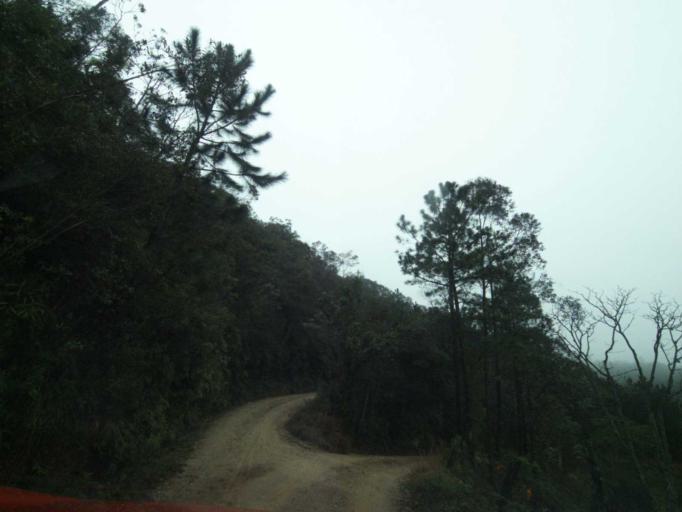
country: BR
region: Santa Catarina
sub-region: Anitapolis
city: Anitapolis
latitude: -27.9207
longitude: -49.1992
